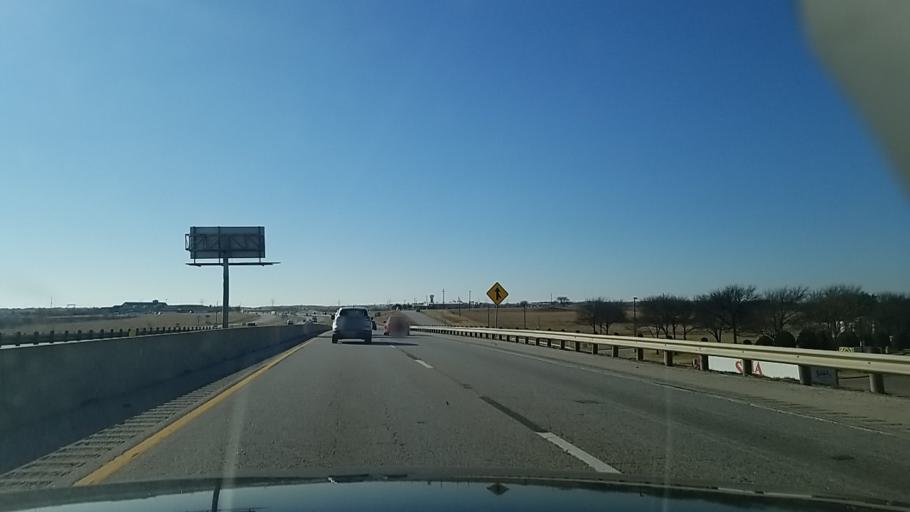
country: US
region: Texas
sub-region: Tarrant County
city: Haslet
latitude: 32.9720
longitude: -97.3092
